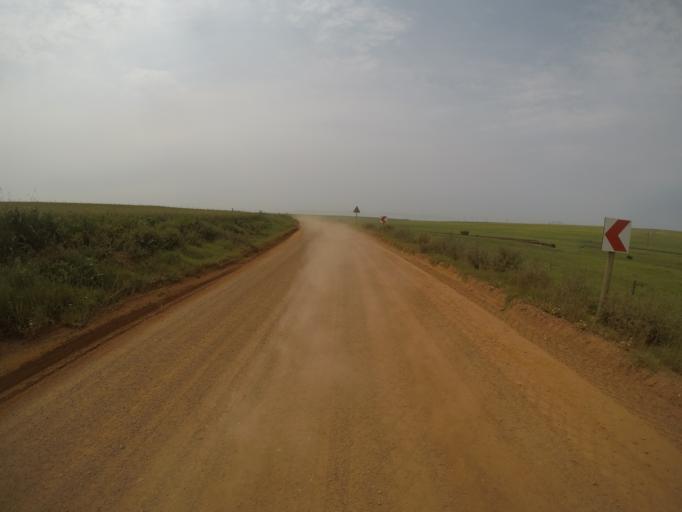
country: ZA
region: Western Cape
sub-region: City of Cape Town
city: Kraaifontein
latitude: -33.7245
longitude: 18.6641
